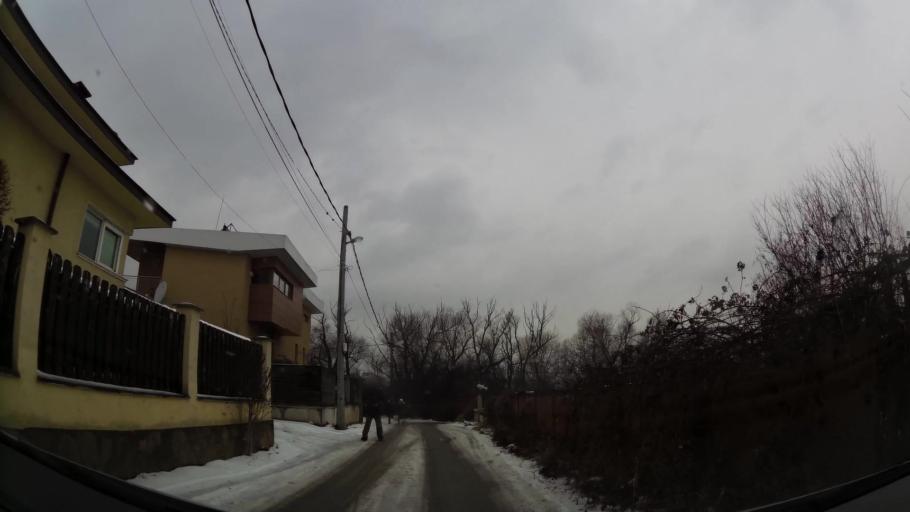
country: BG
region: Sofia-Capital
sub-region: Stolichna Obshtina
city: Sofia
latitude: 42.6514
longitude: 23.2958
